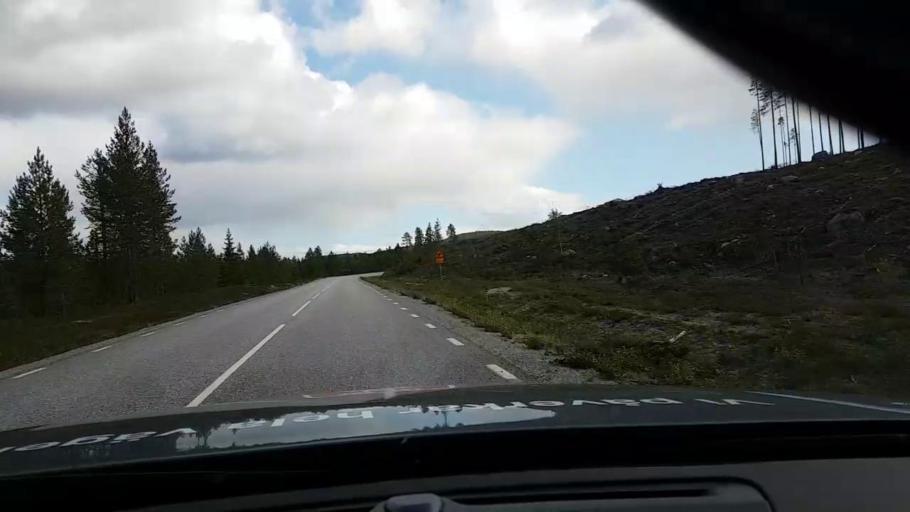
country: SE
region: Vaesternorrland
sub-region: OErnskoeldsviks Kommun
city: Bredbyn
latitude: 63.6793
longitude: 17.7881
